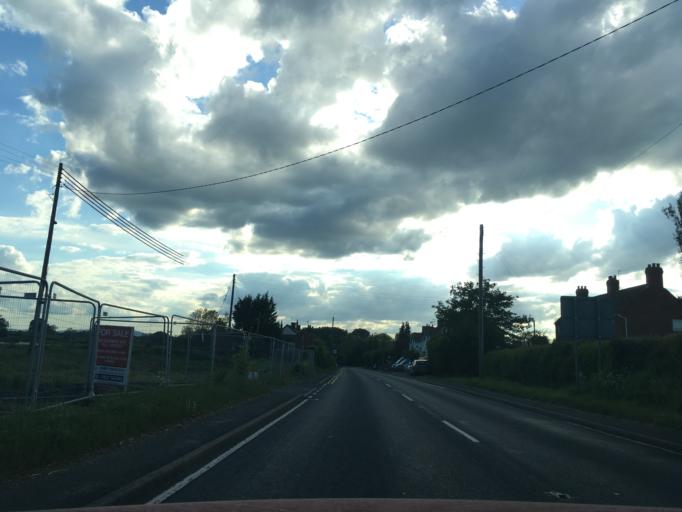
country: GB
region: England
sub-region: Worcestershire
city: Kington
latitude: 52.1888
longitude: -2.0876
